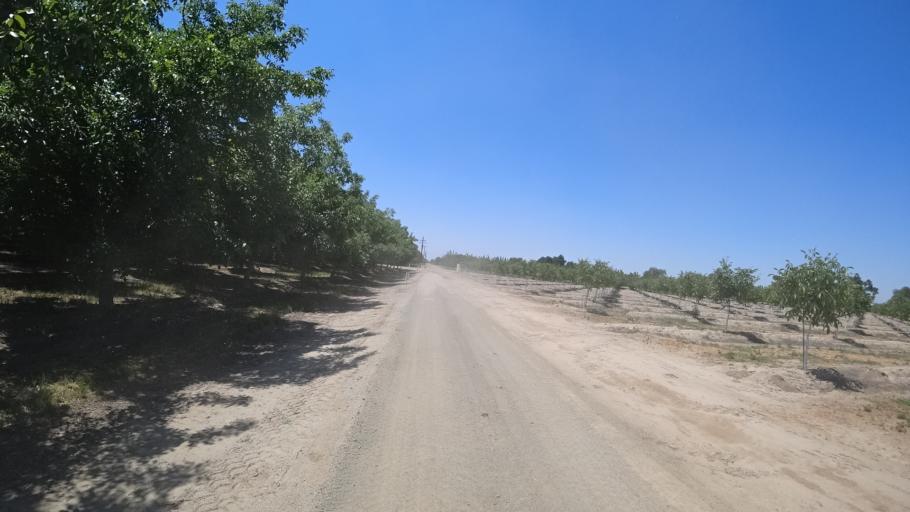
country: US
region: California
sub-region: Kings County
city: Lucerne
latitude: 36.4267
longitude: -119.6129
